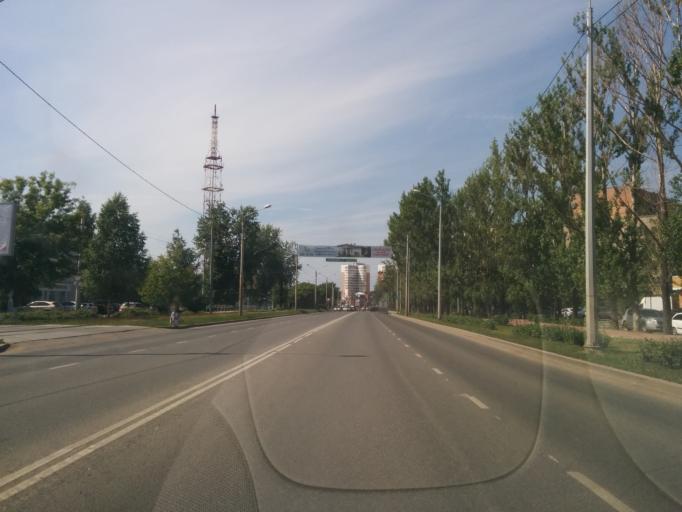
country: RU
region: Perm
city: Perm
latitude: 57.9913
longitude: 56.2947
